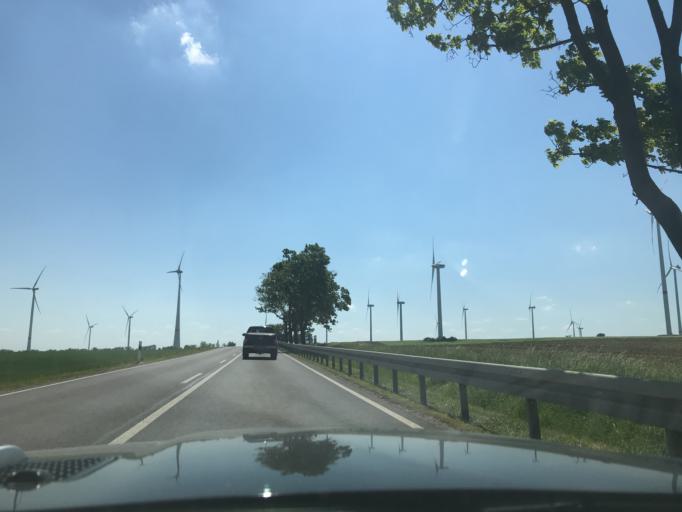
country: DE
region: Thuringia
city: Hochheim
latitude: 51.0458
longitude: 10.6593
